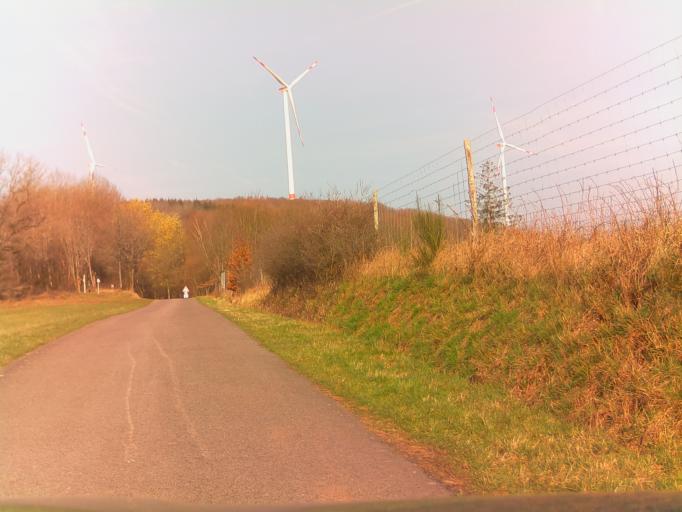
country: DE
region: Rheinland-Pfalz
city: Achtelsbach
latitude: 49.5820
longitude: 7.0554
